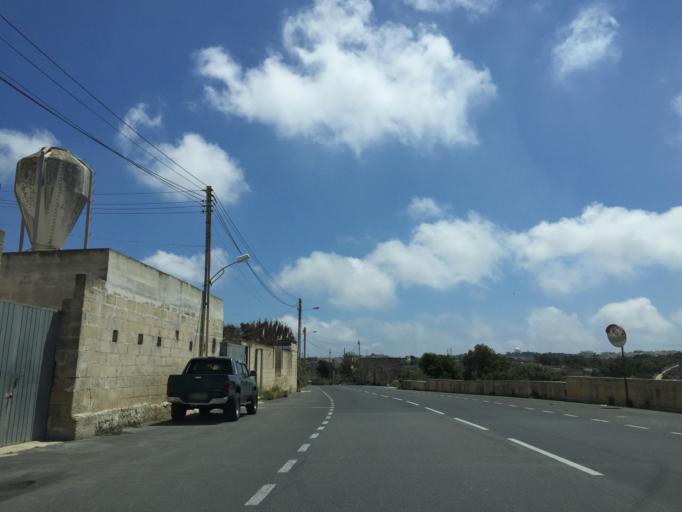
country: MT
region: Dingli
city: Dingli
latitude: 35.8697
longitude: 14.3909
